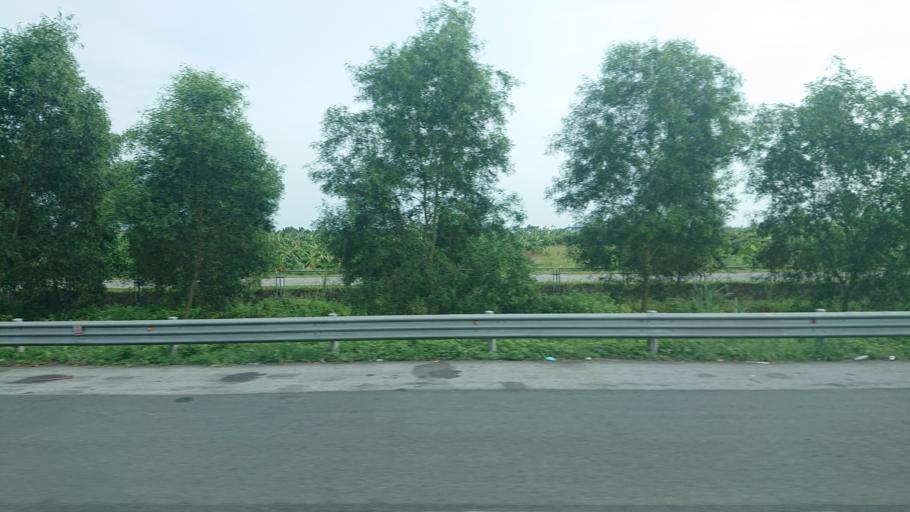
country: VN
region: Hai Phong
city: An Lao
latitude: 20.8160
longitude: 106.4906
